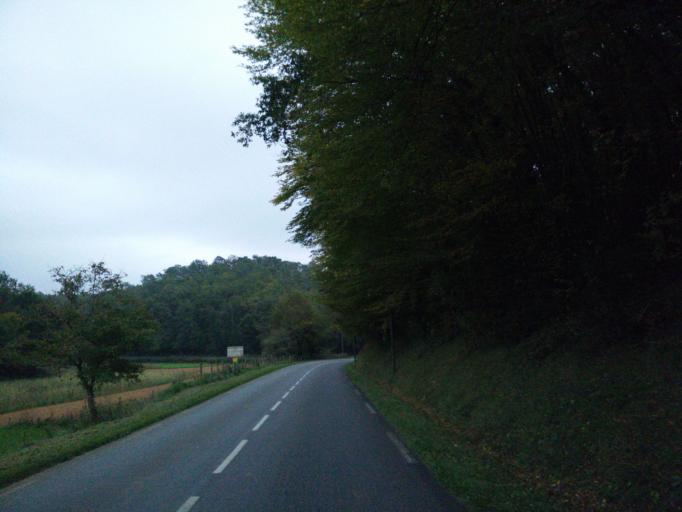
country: FR
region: Midi-Pyrenees
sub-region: Departement du Lot
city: Gourdon
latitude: 44.7711
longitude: 1.3368
